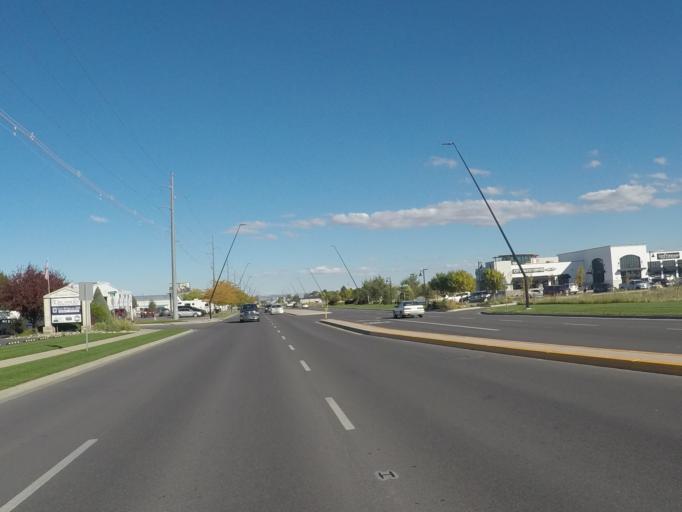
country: US
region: Montana
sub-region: Yellowstone County
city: Billings
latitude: 45.7842
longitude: -108.5991
